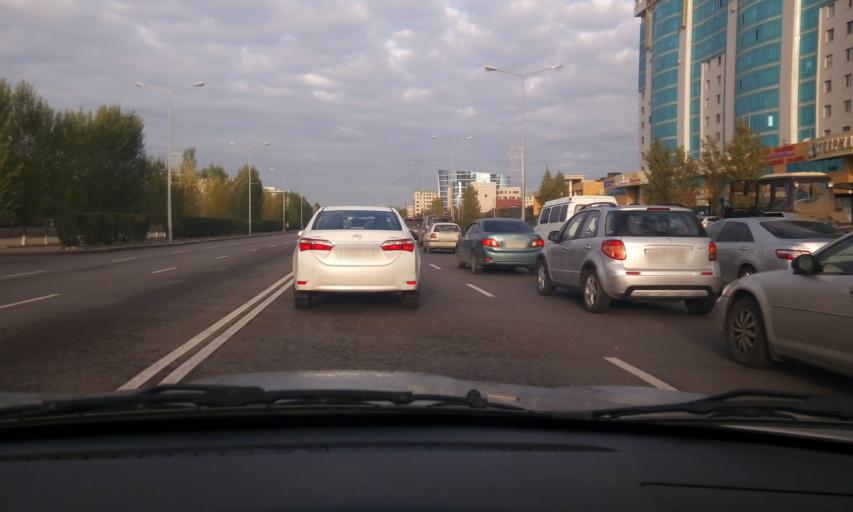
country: KZ
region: Astana Qalasy
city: Astana
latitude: 51.1353
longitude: 71.4233
